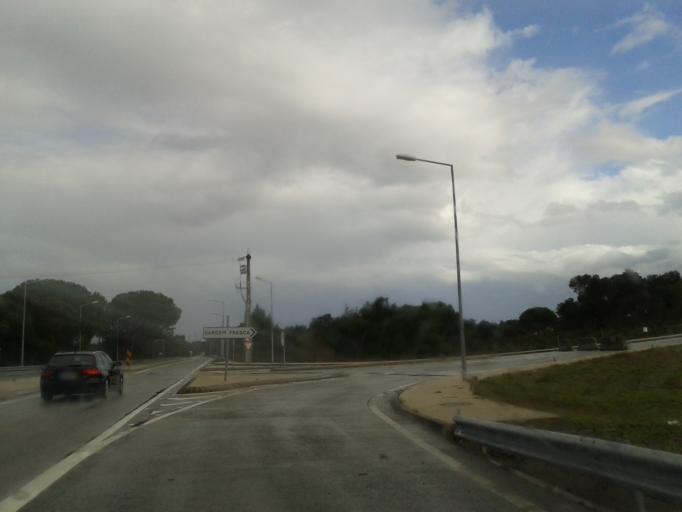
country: PT
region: Santarem
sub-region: Benavente
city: Poceirao
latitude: 38.8295
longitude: -8.7531
